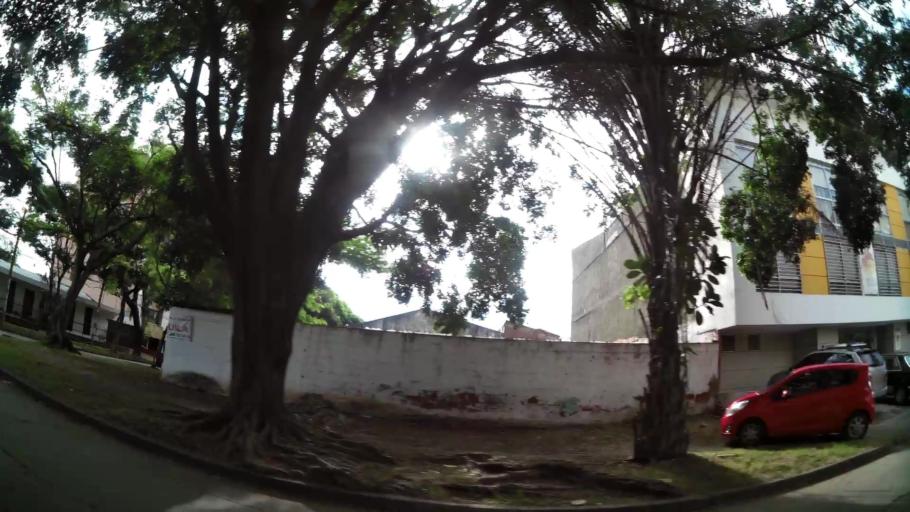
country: CO
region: Valle del Cauca
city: Cali
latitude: 3.4787
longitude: -76.5248
